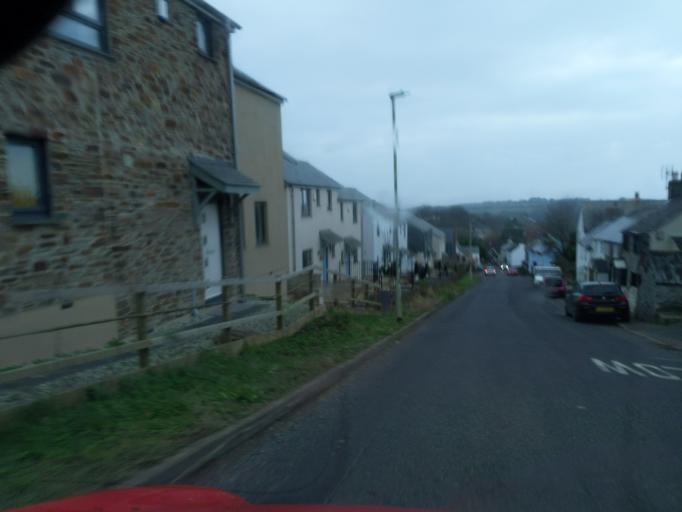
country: GB
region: England
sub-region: Devon
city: Wembury
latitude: 50.3295
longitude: -4.0635
